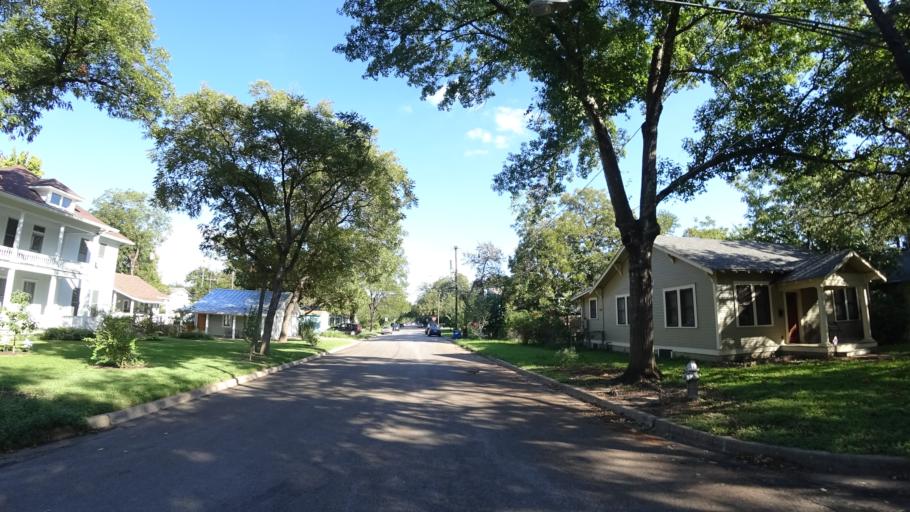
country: US
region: Texas
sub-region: Travis County
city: Austin
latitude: 30.3080
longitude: -97.7300
